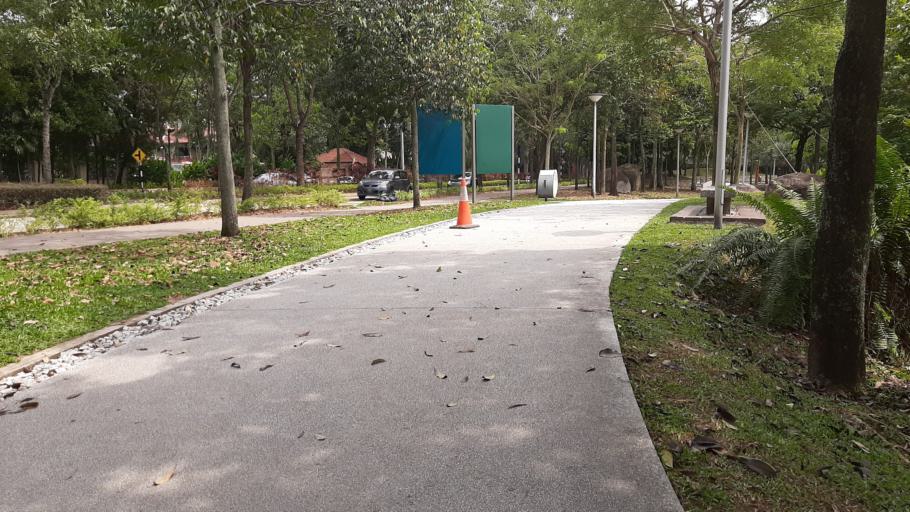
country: MY
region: Kuala Lumpur
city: Kuala Lumpur
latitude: 3.1876
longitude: 101.6290
